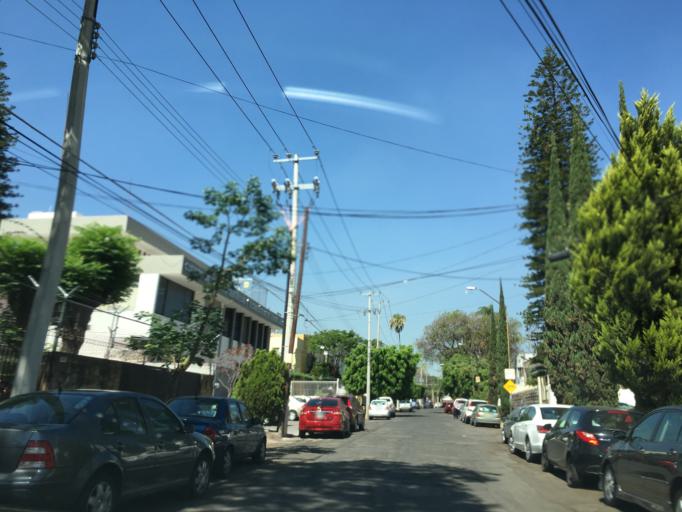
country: MX
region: Jalisco
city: Guadalajara
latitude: 20.6703
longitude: -103.3751
